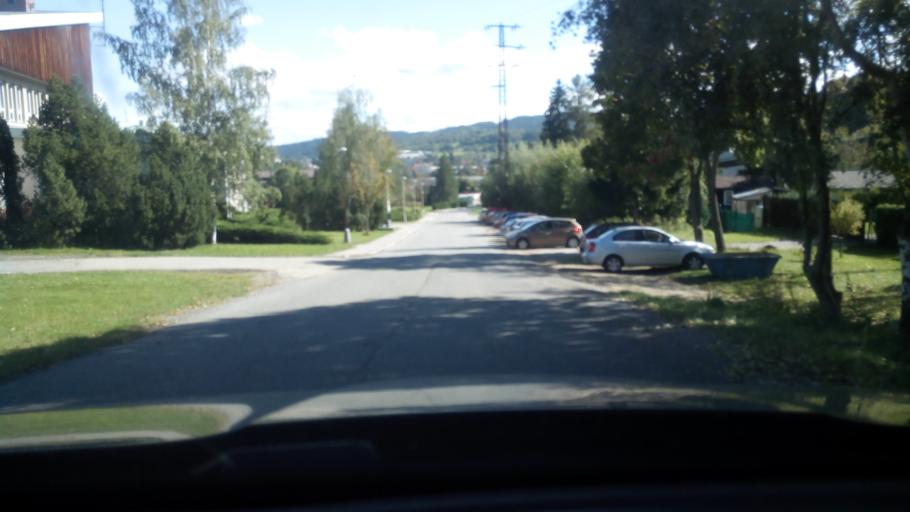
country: CZ
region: Jihocesky
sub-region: Okres Prachatice
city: Vimperk
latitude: 49.0592
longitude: 13.7744
